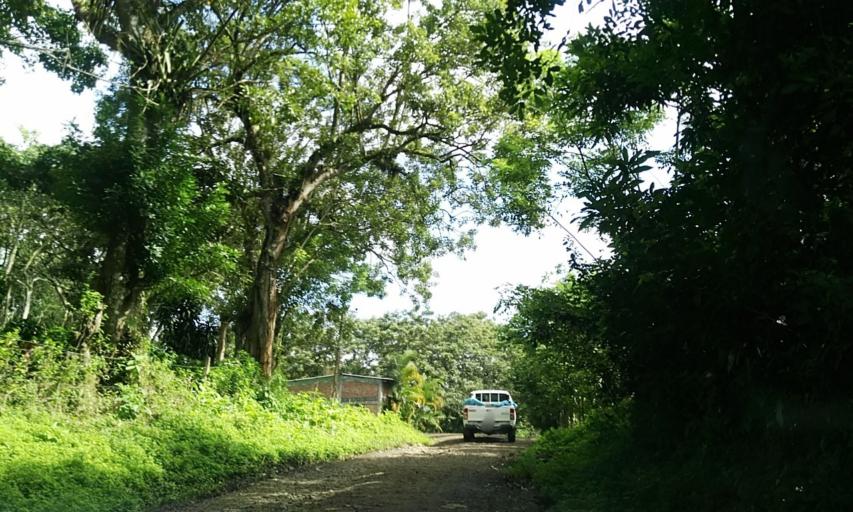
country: NI
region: Matagalpa
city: San Ramon
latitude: 12.9840
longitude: -85.8464
